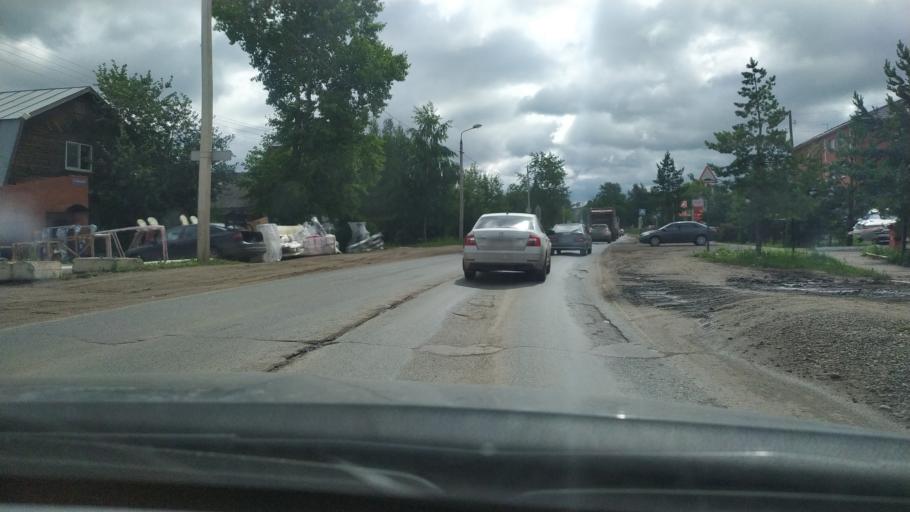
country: RU
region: Perm
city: Froly
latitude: 57.9772
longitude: 56.3129
